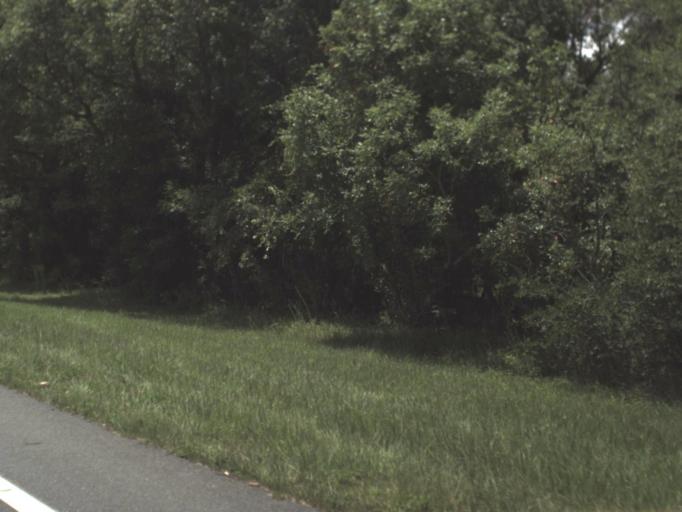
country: US
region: Florida
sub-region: Clay County
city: Keystone Heights
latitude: 29.7566
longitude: -81.9979
